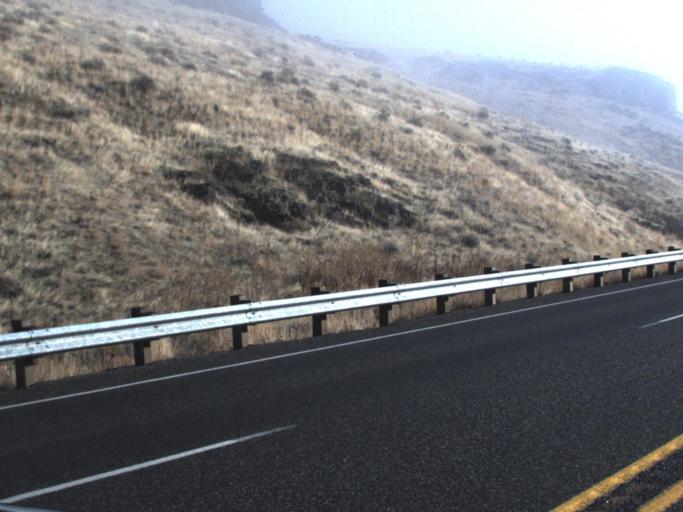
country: US
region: Washington
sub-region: Garfield County
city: Pomeroy
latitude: 46.4348
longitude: -117.3428
